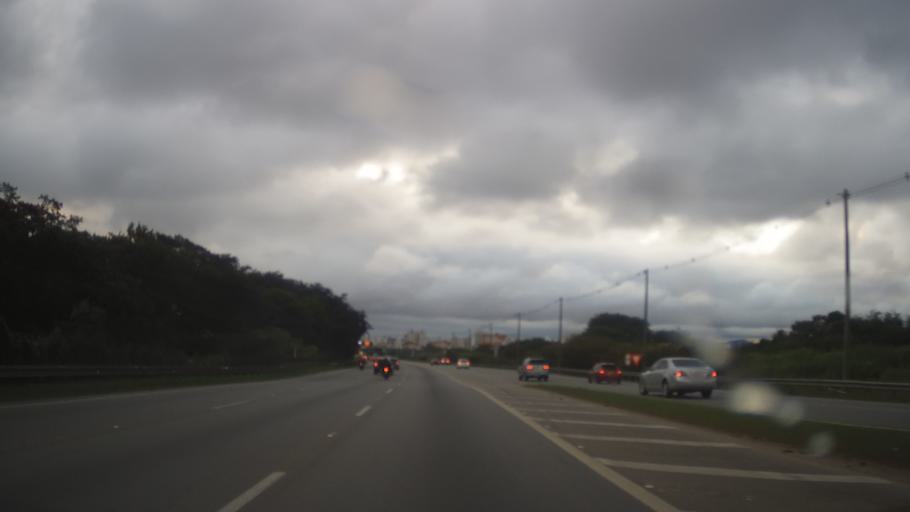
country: BR
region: Sao Paulo
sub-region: Guarulhos
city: Guarulhos
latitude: -23.4718
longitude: -46.4892
